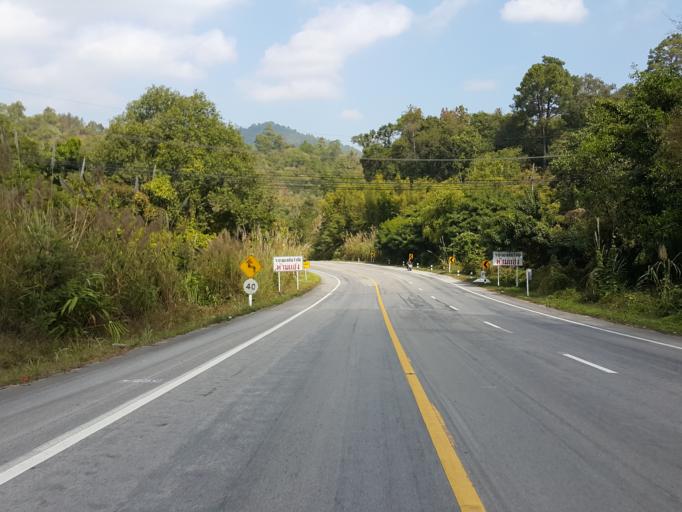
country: TH
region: Lampang
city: Wang Nuea
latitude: 19.0763
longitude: 99.3946
